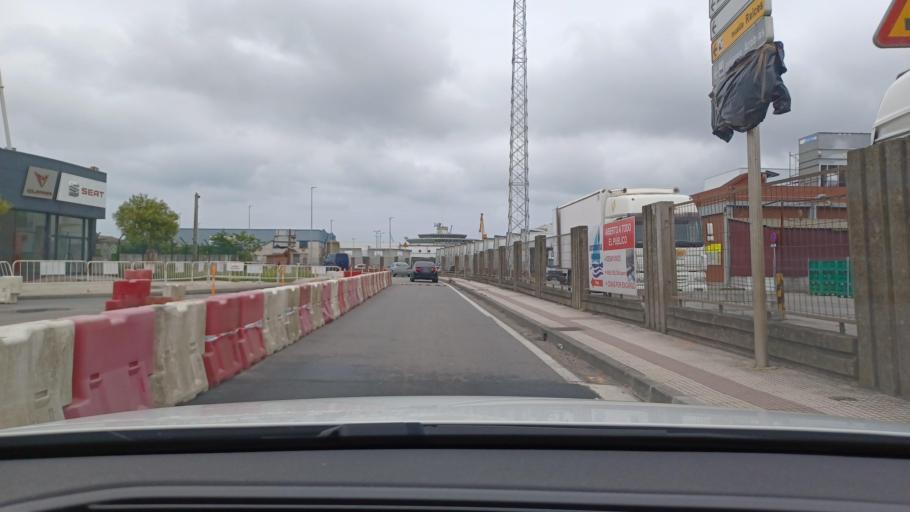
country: ES
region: Asturias
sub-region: Province of Asturias
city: Aviles
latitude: 43.5729
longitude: -5.9231
